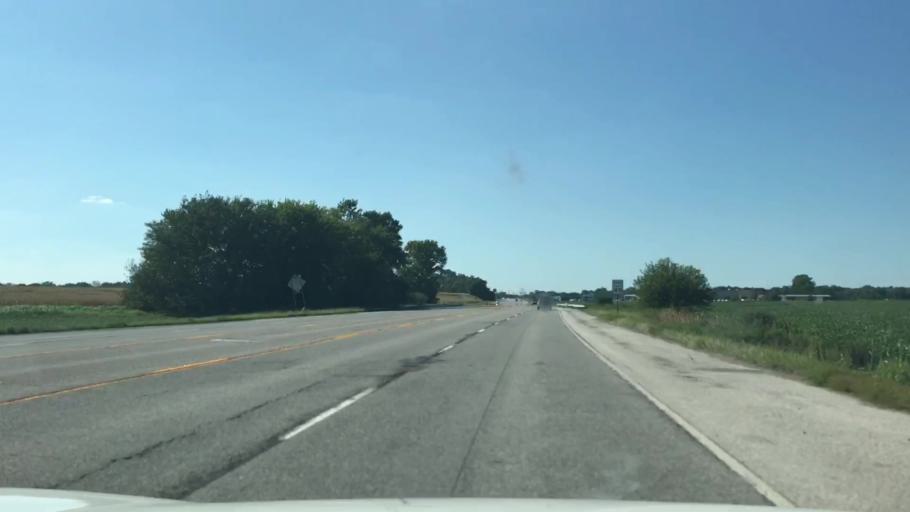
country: US
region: Illinois
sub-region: Madison County
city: Roxana
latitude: 38.8529
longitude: -90.0568
